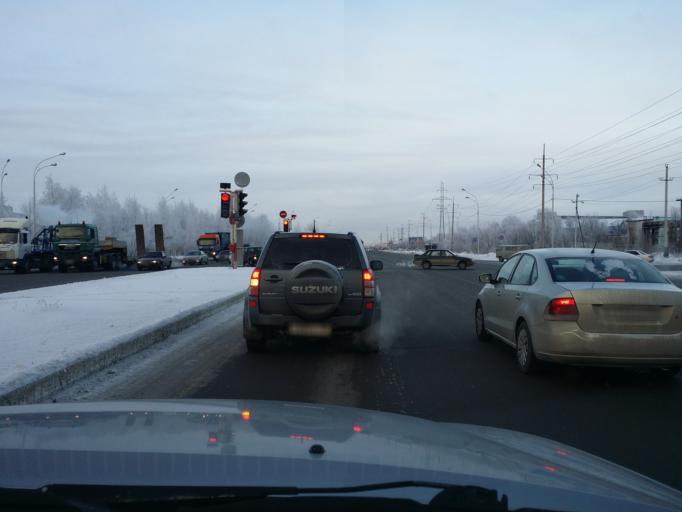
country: RU
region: Khanty-Mansiyskiy Avtonomnyy Okrug
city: Nizhnevartovsk
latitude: 60.9478
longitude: 76.5296
